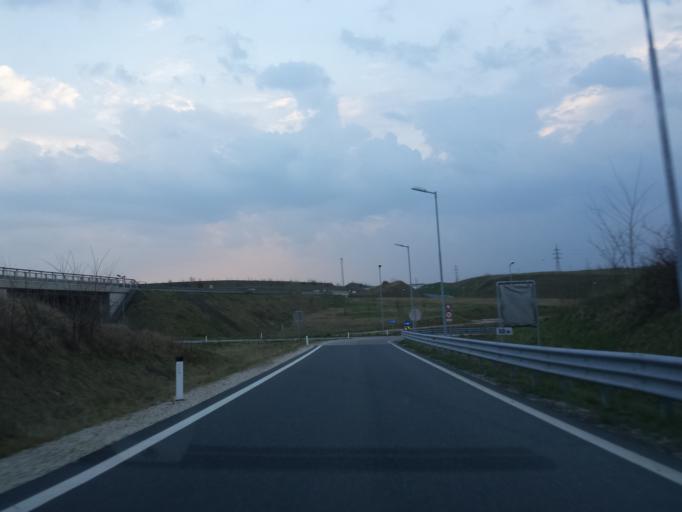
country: AT
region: Lower Austria
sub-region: Politischer Bezirk Mistelbach
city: Gaweinstal
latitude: 48.5190
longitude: 16.6213
